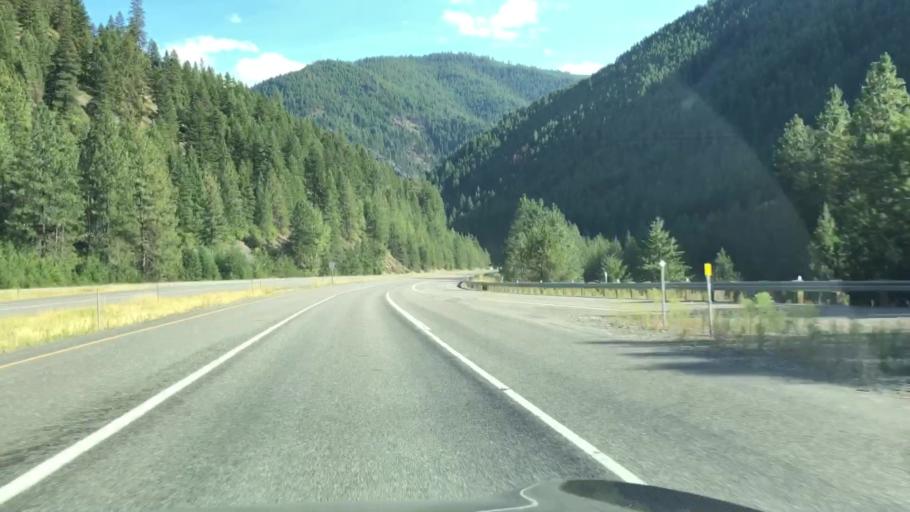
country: US
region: Montana
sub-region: Sanders County
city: Thompson Falls
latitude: 47.3208
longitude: -115.2462
